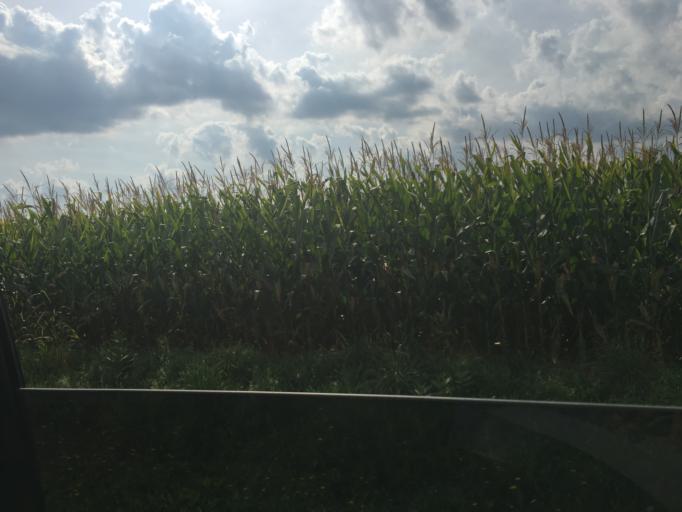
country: US
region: New York
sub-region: Madison County
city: Cazenovia
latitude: 42.9822
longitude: -75.7809
